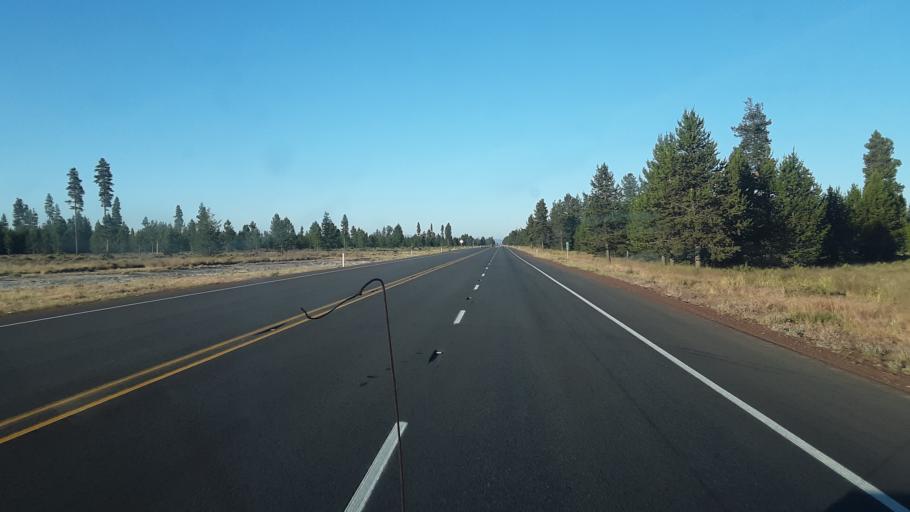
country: US
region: Oregon
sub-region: Deschutes County
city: La Pine
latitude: 43.6947
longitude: -121.4839
